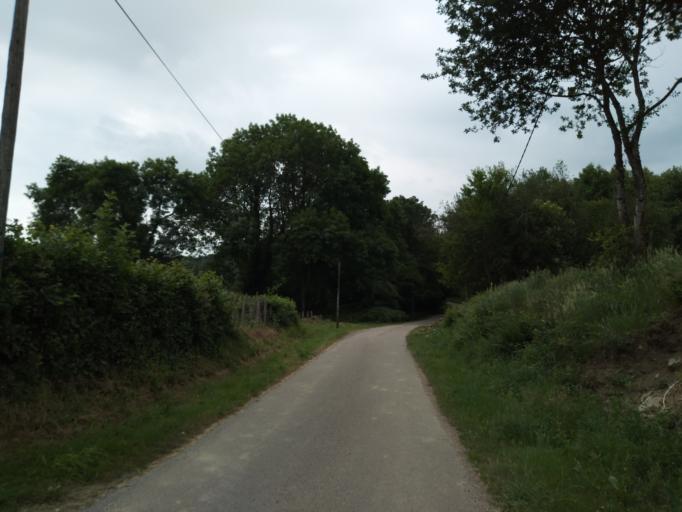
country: FR
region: Bourgogne
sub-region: Departement de la Cote-d'Or
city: Saulieu
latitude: 47.2822
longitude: 4.1218
